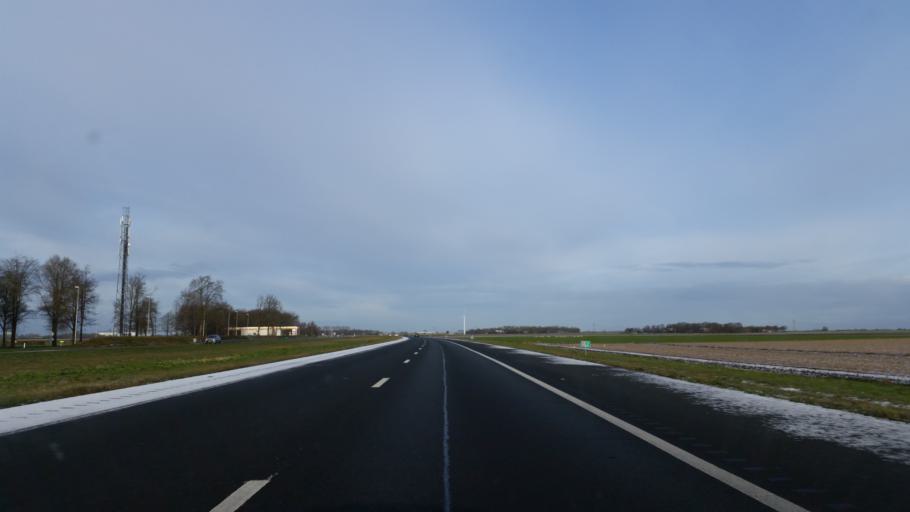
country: NL
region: Friesland
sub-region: Gemeente Lemsterland
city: Lemmer
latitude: 52.8146
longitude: 5.7458
